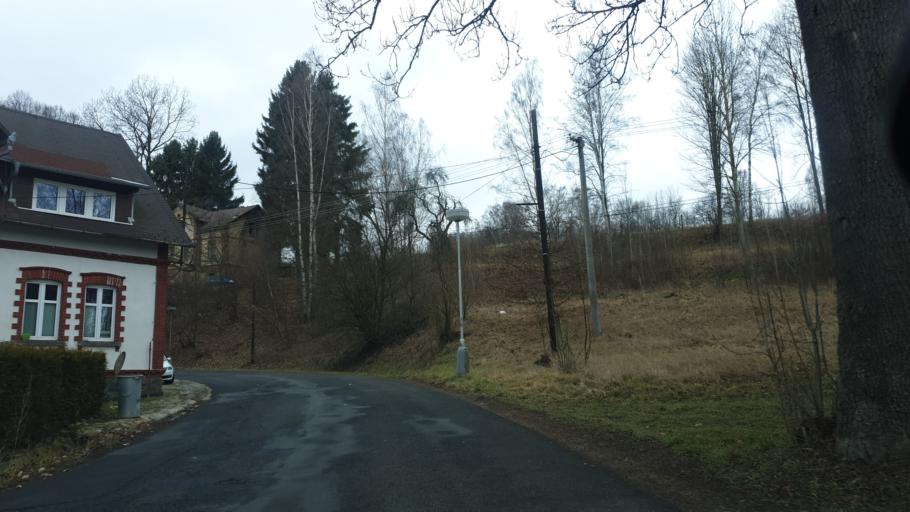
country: DE
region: Saxony
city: Bad Elster
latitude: 50.2610
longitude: 12.2388
